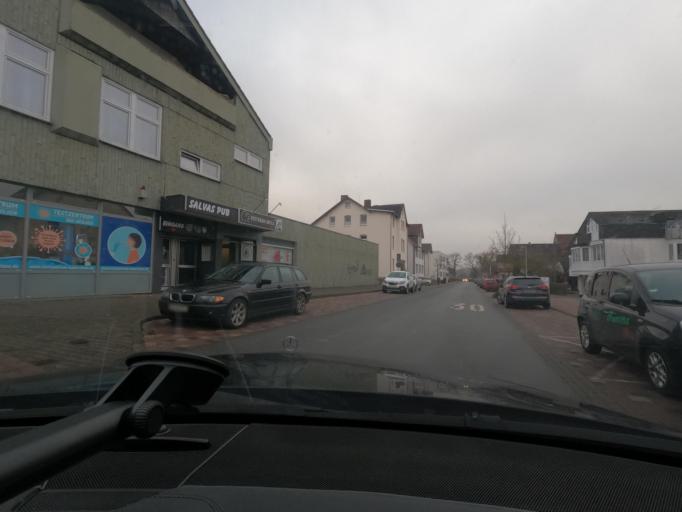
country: DE
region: Hesse
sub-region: Regierungsbezirk Kassel
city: Bad Arolsen
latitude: 51.3809
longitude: 9.0093
